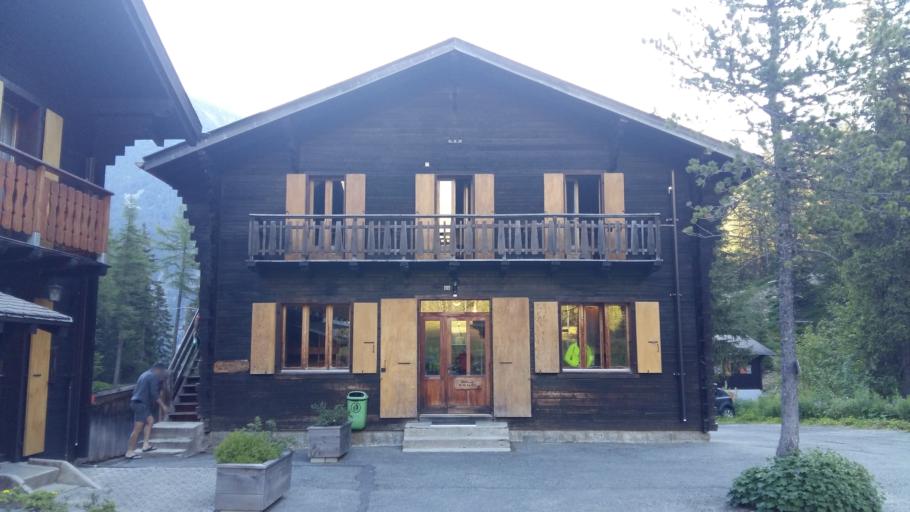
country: CH
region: Valais
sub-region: Entremont District
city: Orsieres
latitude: 46.0292
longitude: 7.0897
